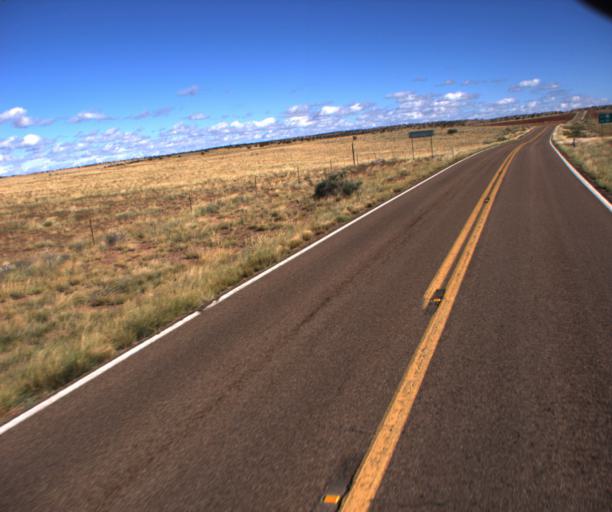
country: US
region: Arizona
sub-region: Apache County
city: Saint Johns
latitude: 34.6381
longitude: -109.3082
